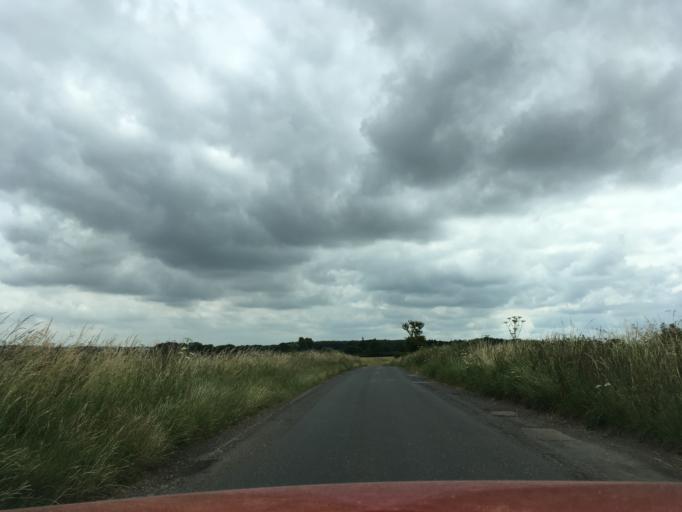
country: GB
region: England
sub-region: Oxfordshire
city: Charlbury
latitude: 51.9161
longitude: -1.4725
